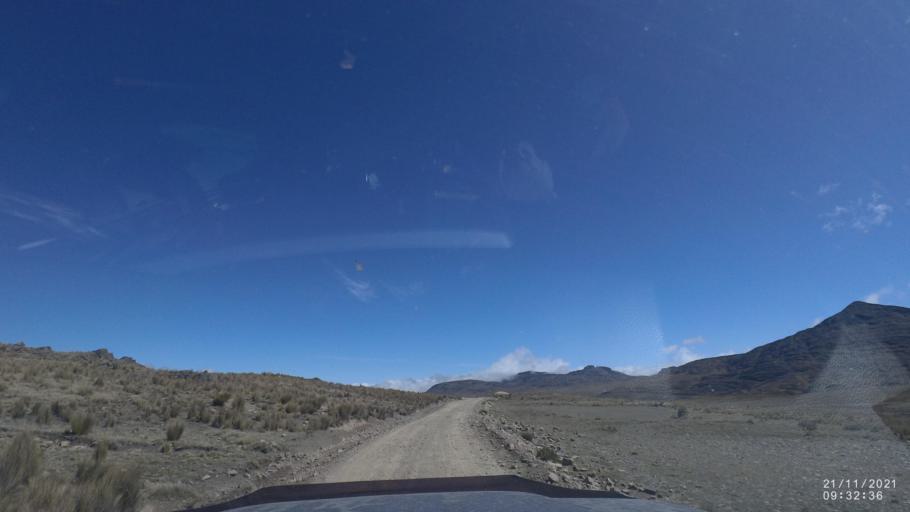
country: BO
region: Cochabamba
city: Cochabamba
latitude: -17.0659
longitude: -66.2563
